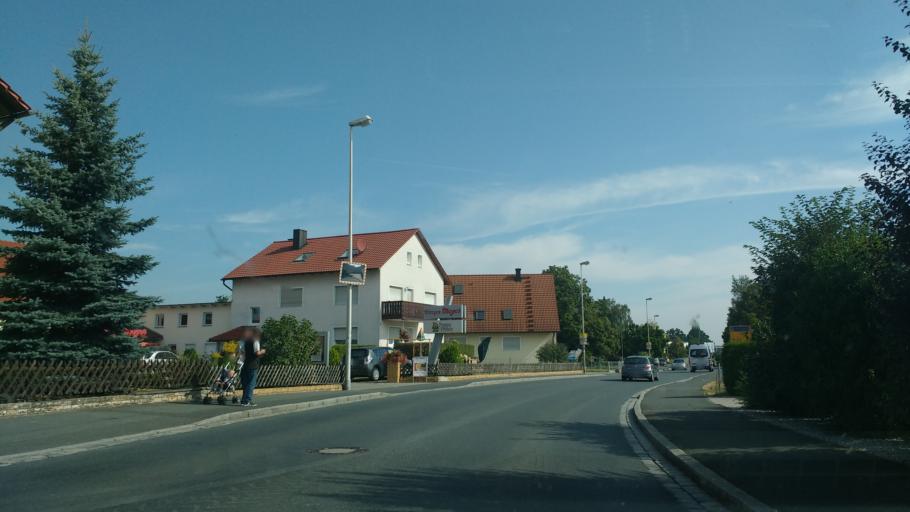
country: DE
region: Bavaria
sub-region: Regierungsbezirk Mittelfranken
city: Grossenseebach
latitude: 49.6322
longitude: 10.8767
